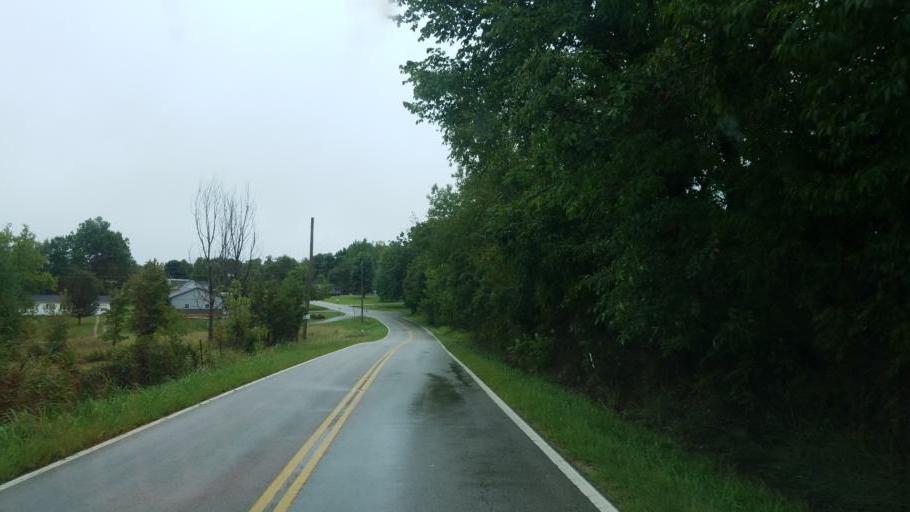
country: US
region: Ohio
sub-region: Adams County
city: West Union
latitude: 38.7293
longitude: -83.5178
